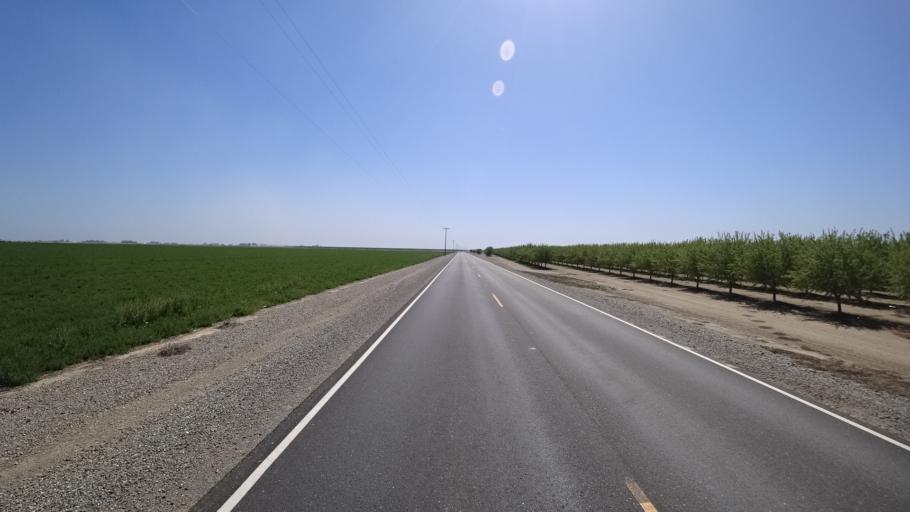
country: US
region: California
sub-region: Glenn County
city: Willows
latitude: 39.6021
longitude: -122.1376
